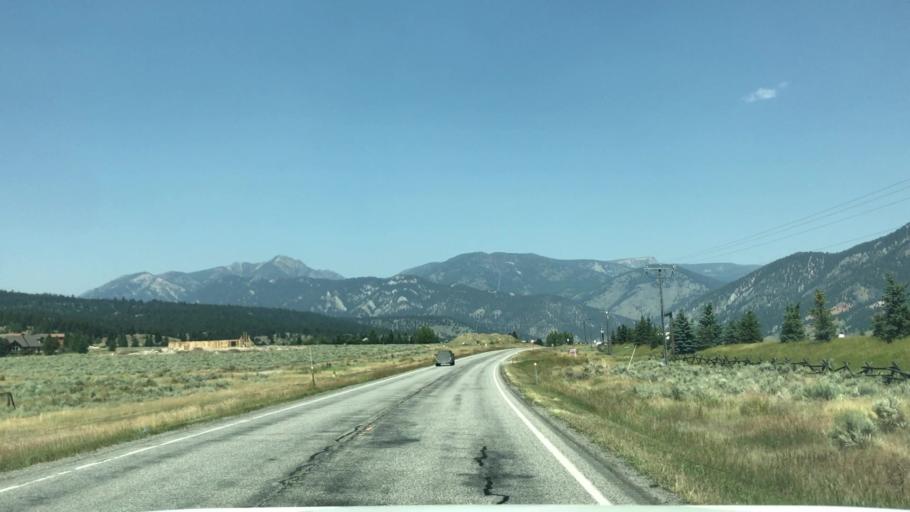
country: US
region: Montana
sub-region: Gallatin County
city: Big Sky
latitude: 45.2197
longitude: -111.2502
